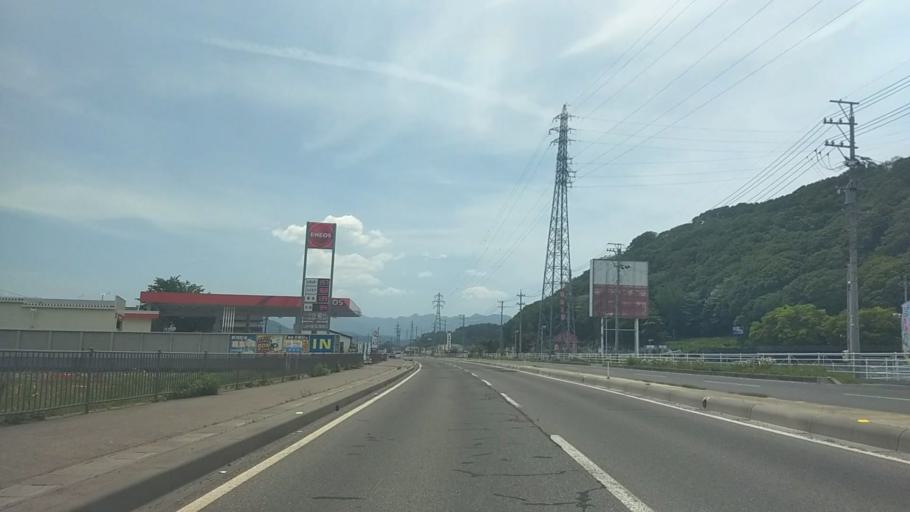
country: JP
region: Nagano
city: Saku
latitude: 36.2033
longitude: 138.4685
